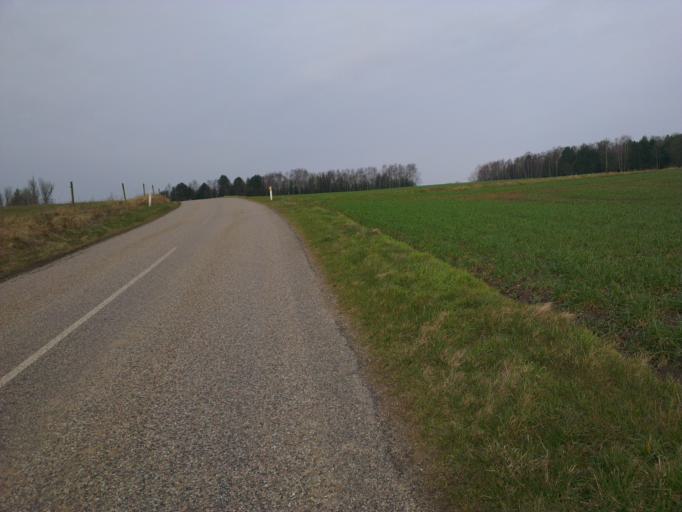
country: DK
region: Capital Region
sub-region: Frederikssund Kommune
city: Skibby
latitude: 55.7613
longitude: 11.8988
